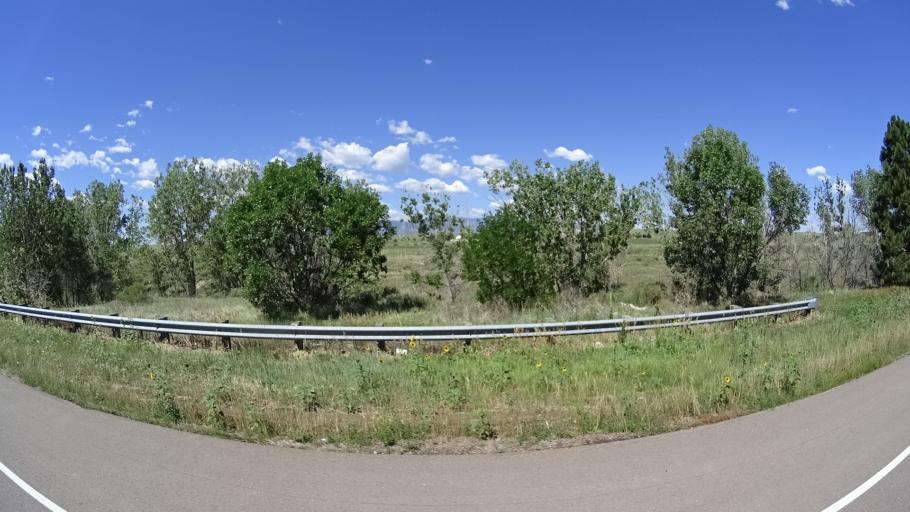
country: US
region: Colorado
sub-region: El Paso County
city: Security-Widefield
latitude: 38.7640
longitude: -104.6598
